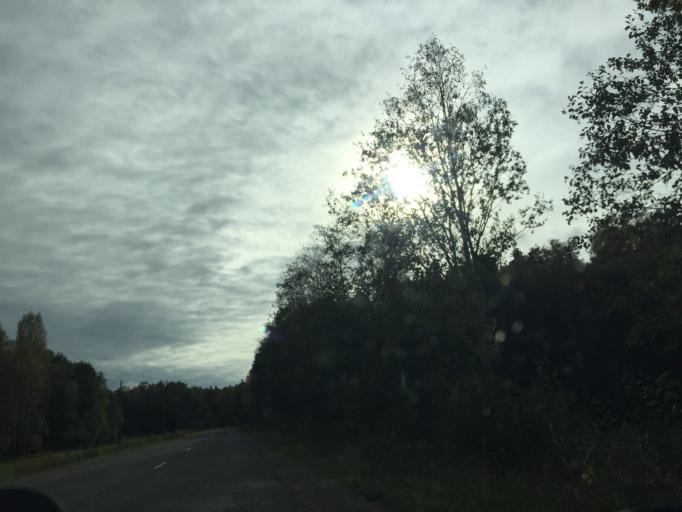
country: LV
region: Auces Novads
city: Auce
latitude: 56.5564
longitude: 23.0183
